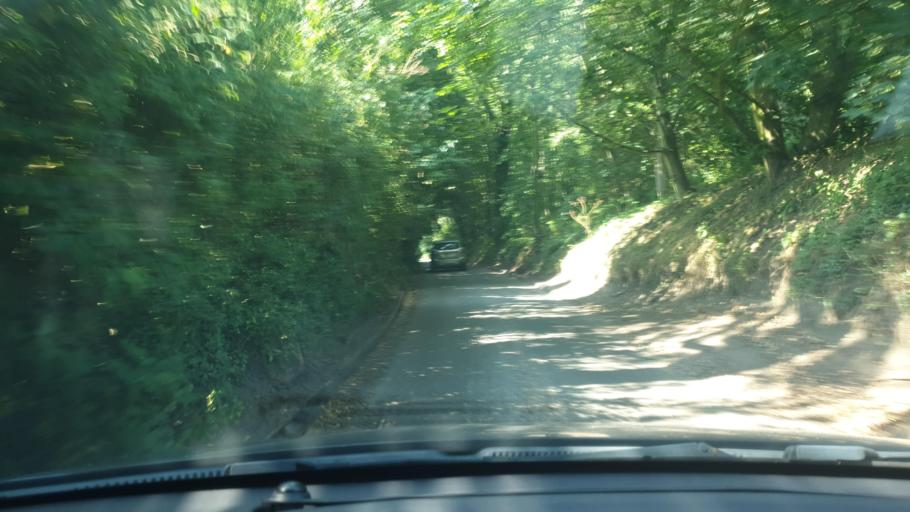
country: GB
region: England
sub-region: Suffolk
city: East Bergholt
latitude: 51.9445
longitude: 1.0249
